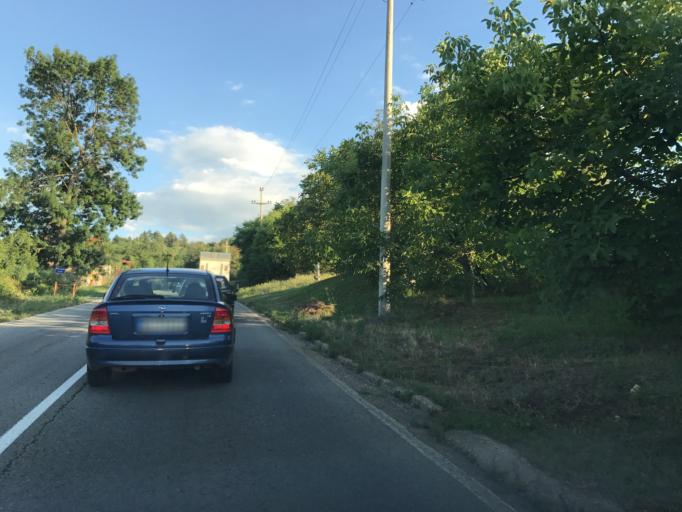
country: RS
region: Central Serbia
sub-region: Belgrade
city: Grocka
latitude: 44.6546
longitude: 20.7470
